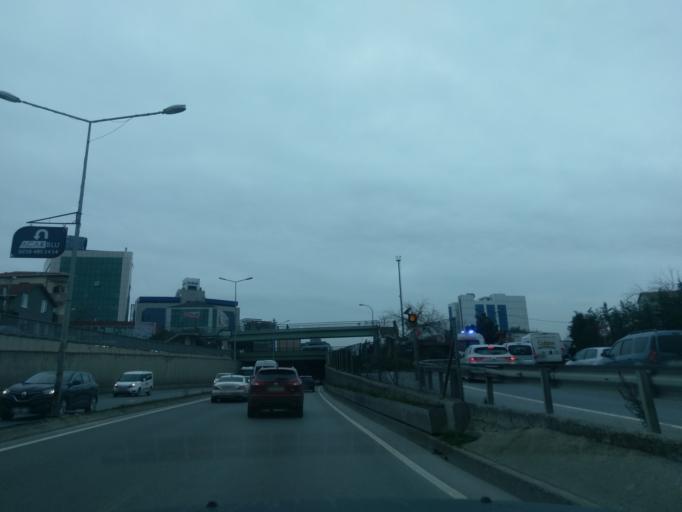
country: TR
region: Istanbul
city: Umraniye
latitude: 41.0968
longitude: 29.0971
